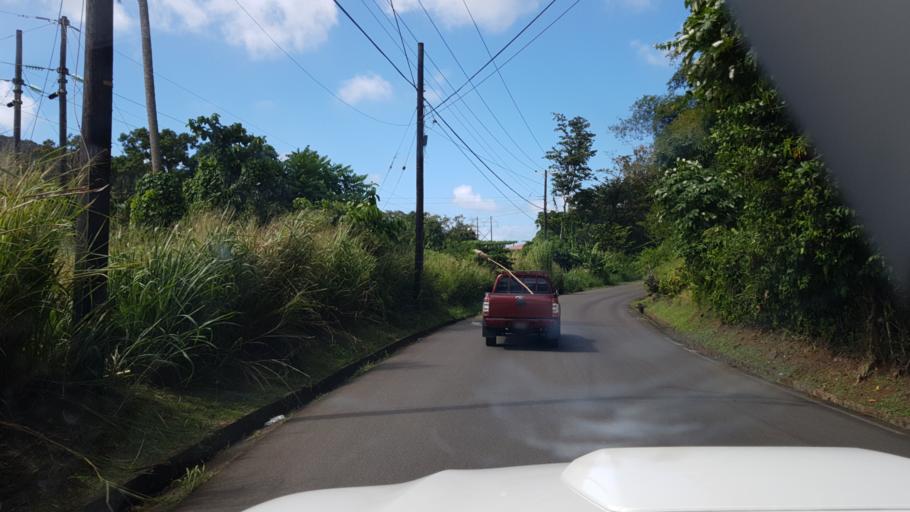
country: LC
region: Castries Quarter
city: Bisee
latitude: 14.0186
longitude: -60.9593
